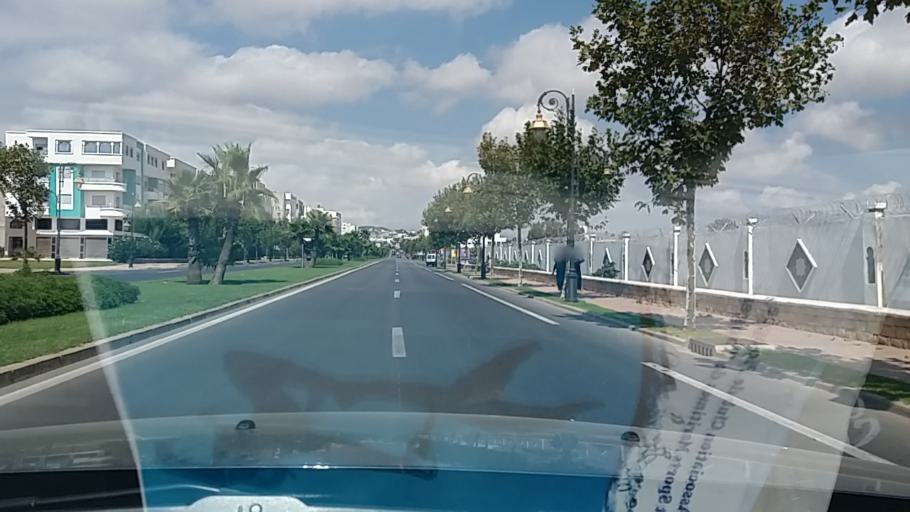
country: MA
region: Tanger-Tetouan
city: Tetouan
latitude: 35.5862
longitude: -5.3331
